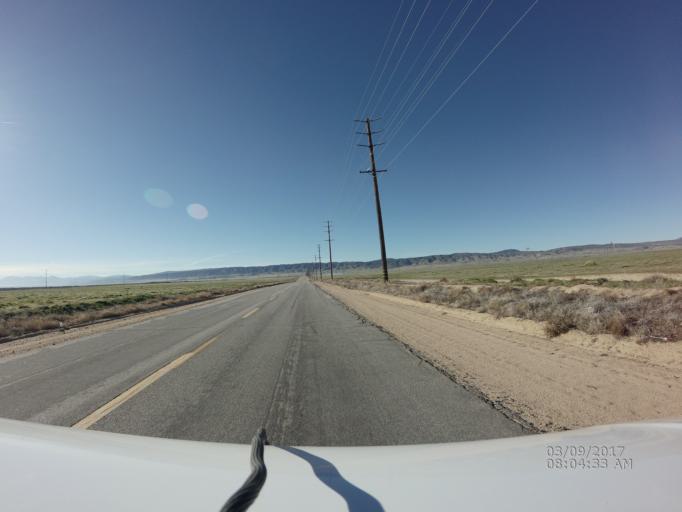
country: US
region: California
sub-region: Los Angeles County
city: Leona Valley
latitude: 34.7303
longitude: -118.3245
